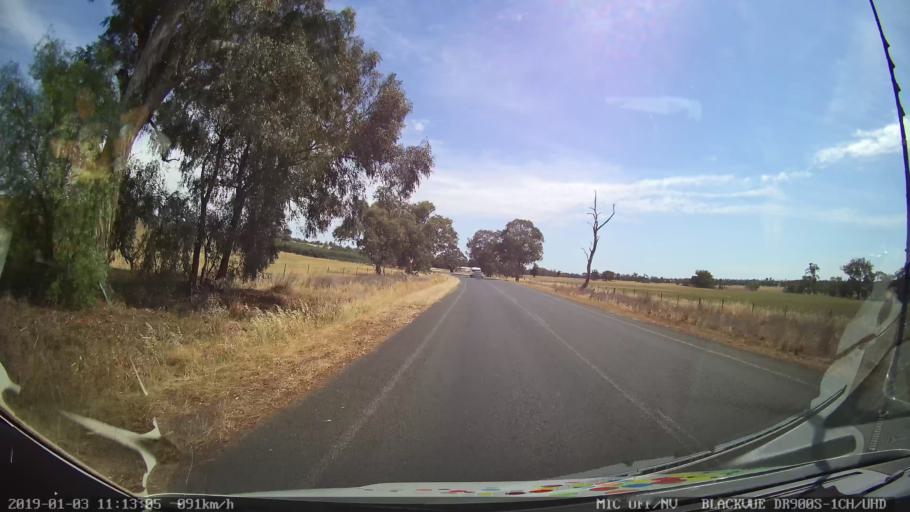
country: AU
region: New South Wales
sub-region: Young
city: Young
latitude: -34.1932
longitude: 148.2615
